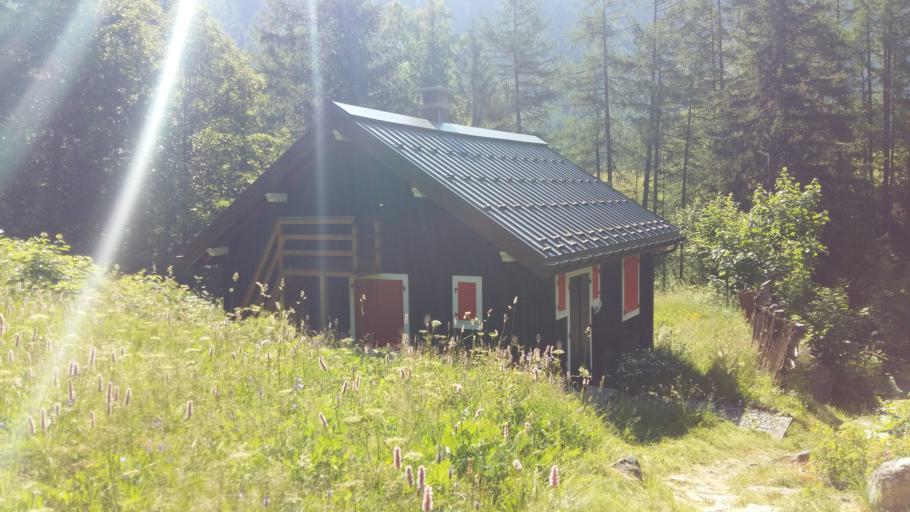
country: FR
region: Rhone-Alpes
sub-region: Departement de la Haute-Savoie
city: Chamonix-Mont-Blanc
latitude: 46.0207
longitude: 6.9163
